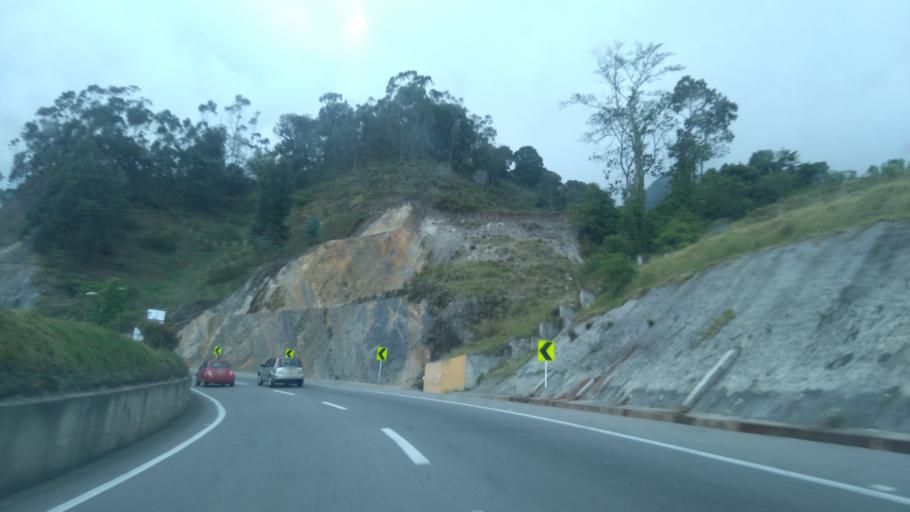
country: CO
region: Cundinamarca
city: El Rosal
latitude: 4.8915
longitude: -74.3056
